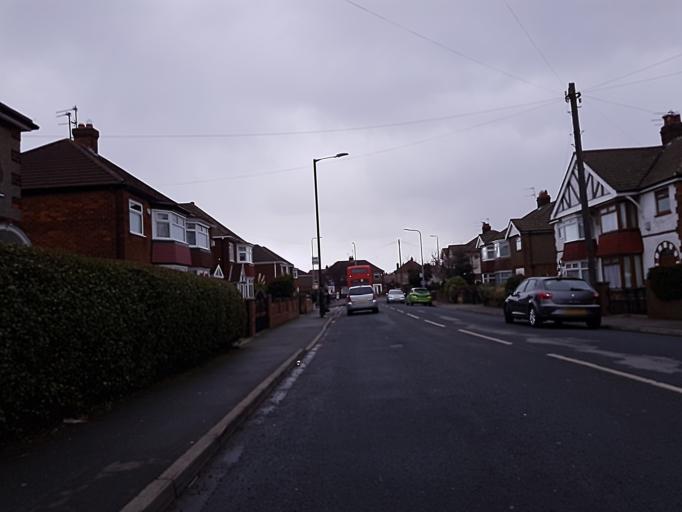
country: GB
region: England
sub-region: North East Lincolnshire
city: Grimbsy
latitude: 53.5617
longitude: -0.1054
